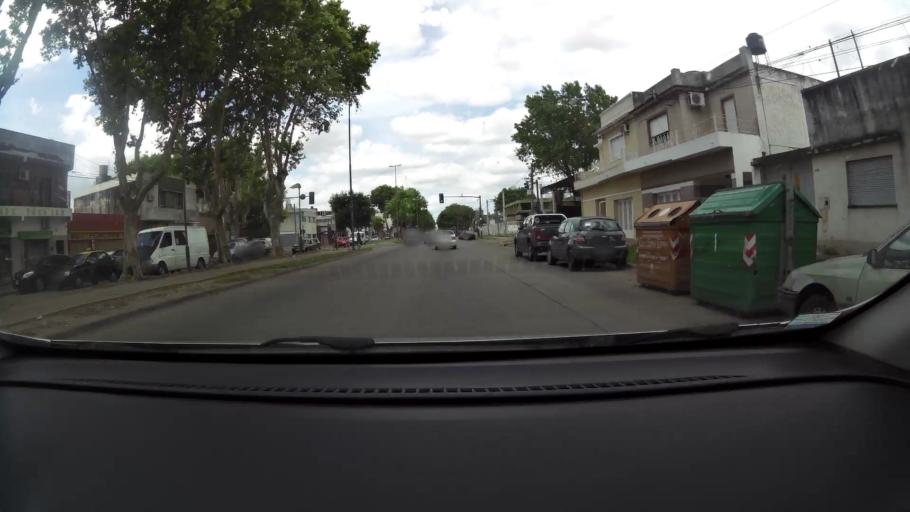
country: AR
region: Santa Fe
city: Gobernador Galvez
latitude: -32.9910
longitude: -60.6528
